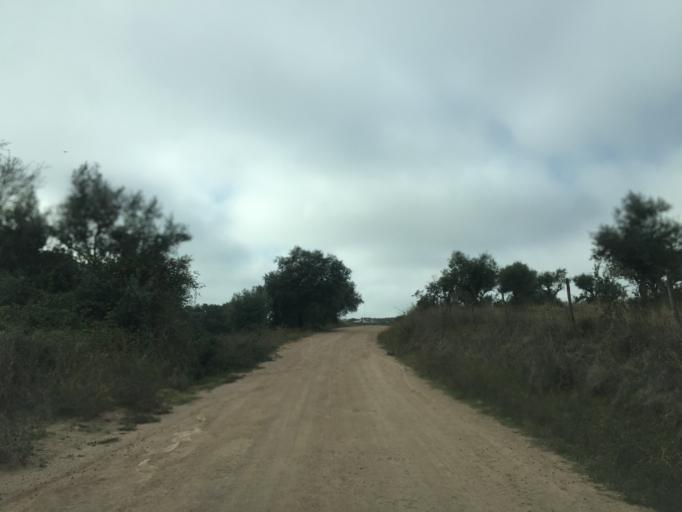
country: PT
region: Portalegre
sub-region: Fronteira
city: Fronteira
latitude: 39.0561
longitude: -7.6341
